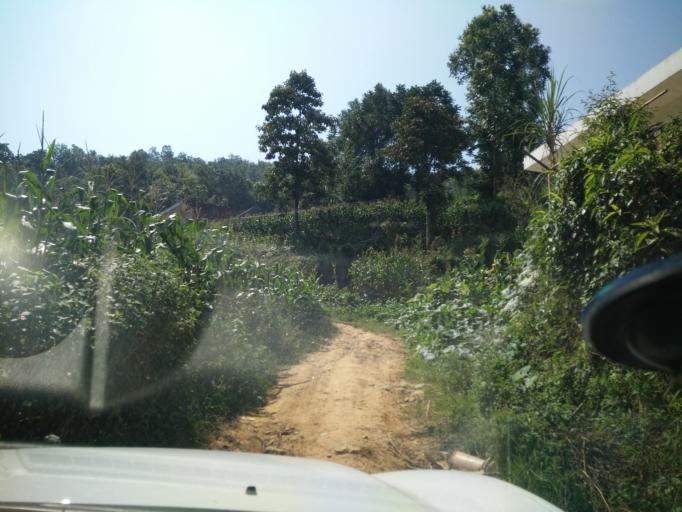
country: CN
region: Guangxi Zhuangzu Zizhiqu
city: Xinzhou
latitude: 25.1847
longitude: 105.6950
